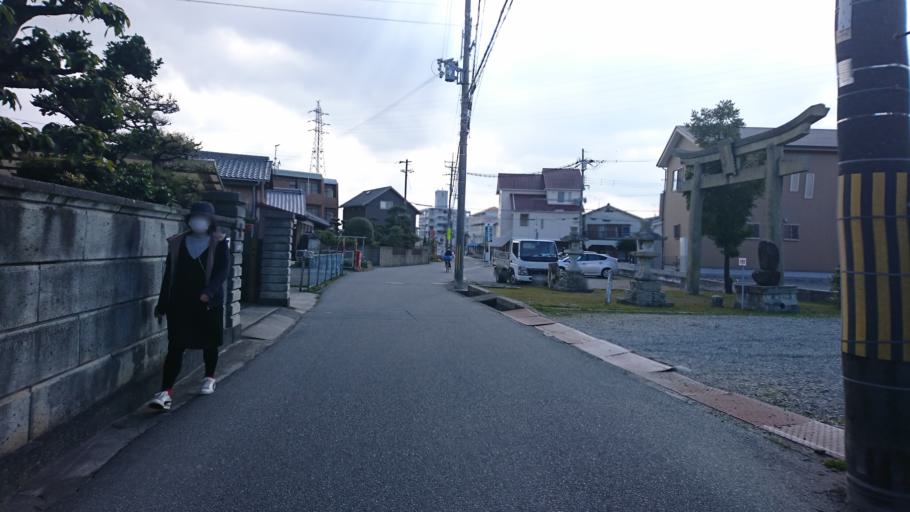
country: JP
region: Hyogo
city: Kakogawacho-honmachi
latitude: 34.7886
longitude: 134.8067
